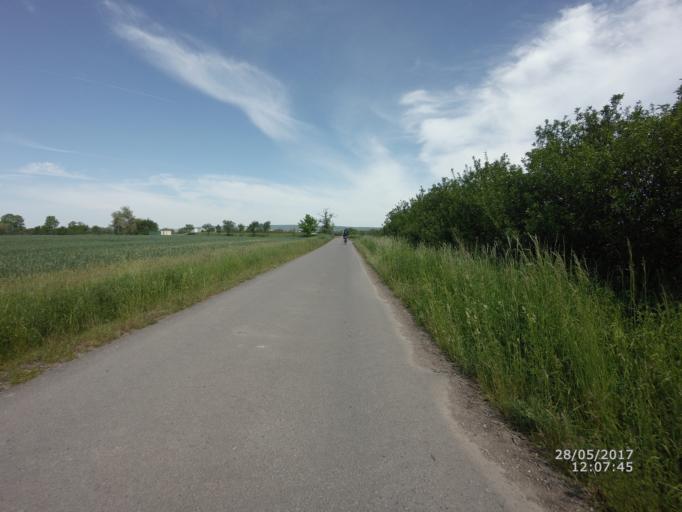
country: DE
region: Thuringia
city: Buchel
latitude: 51.2499
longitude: 11.1624
